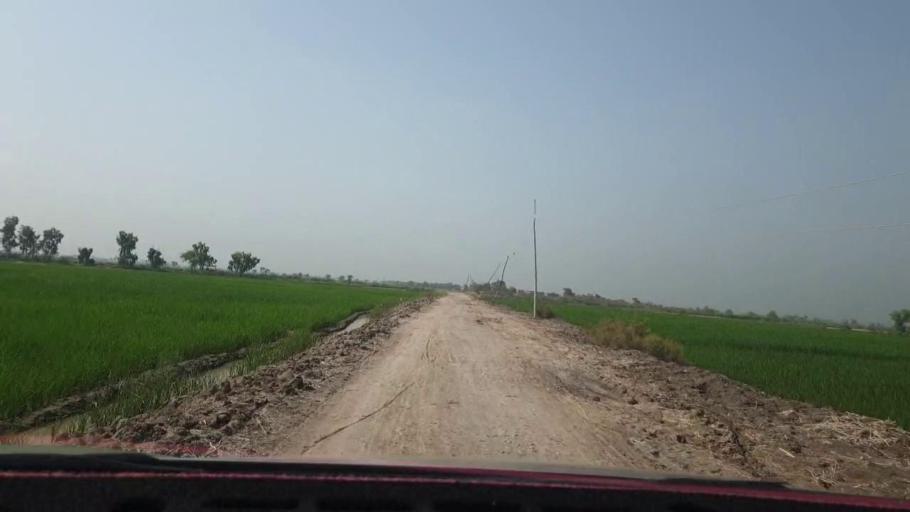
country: PK
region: Sindh
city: Nasirabad
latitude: 27.4329
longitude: 67.9554
